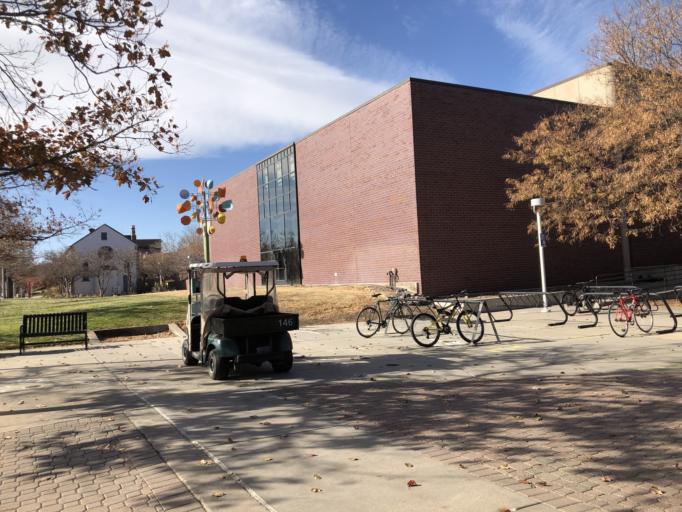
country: US
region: Colorado
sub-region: Denver County
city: Denver
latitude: 39.7444
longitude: -105.0029
